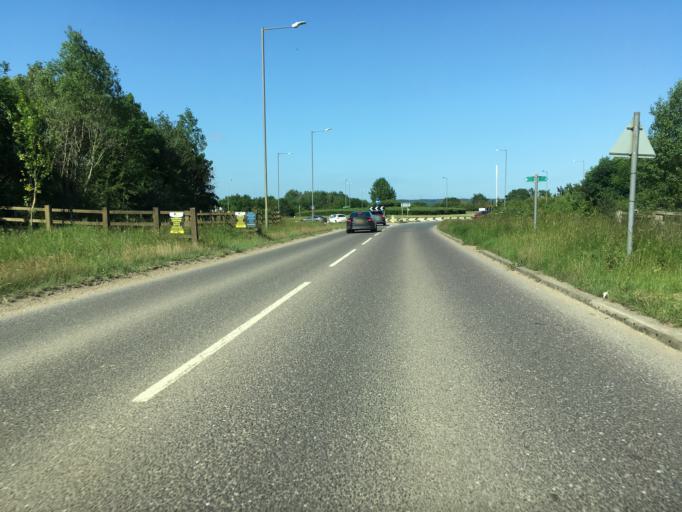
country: GB
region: England
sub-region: Milton Keynes
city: Water Eaton
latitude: 51.9710
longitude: -0.7315
